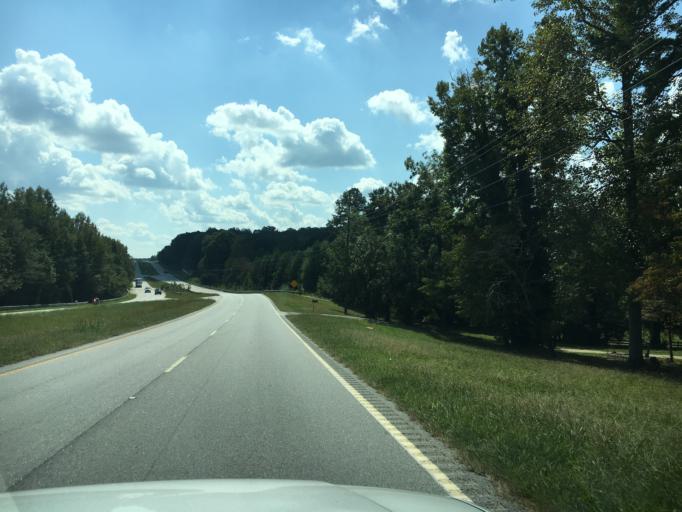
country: US
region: South Carolina
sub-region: Spartanburg County
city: Woodruff
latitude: 34.7916
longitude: -82.0213
